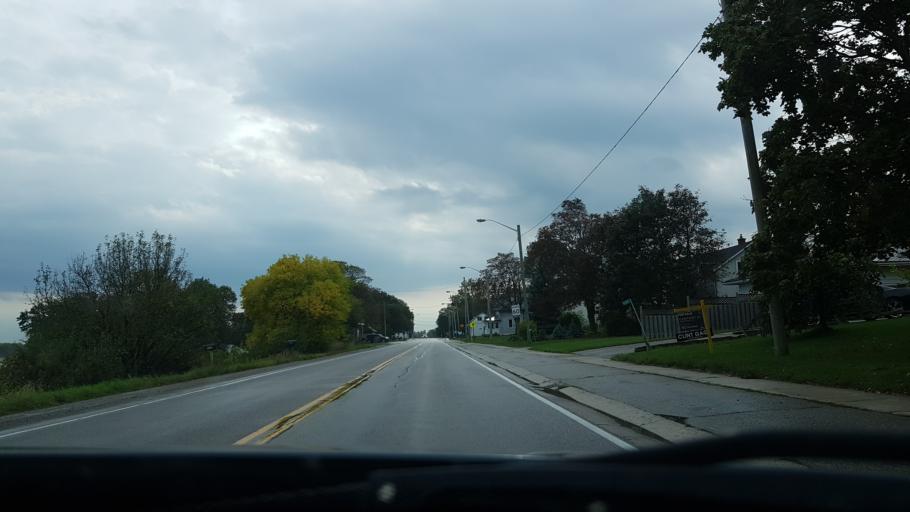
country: CA
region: Ontario
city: Omemee
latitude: 44.4415
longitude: -78.7730
